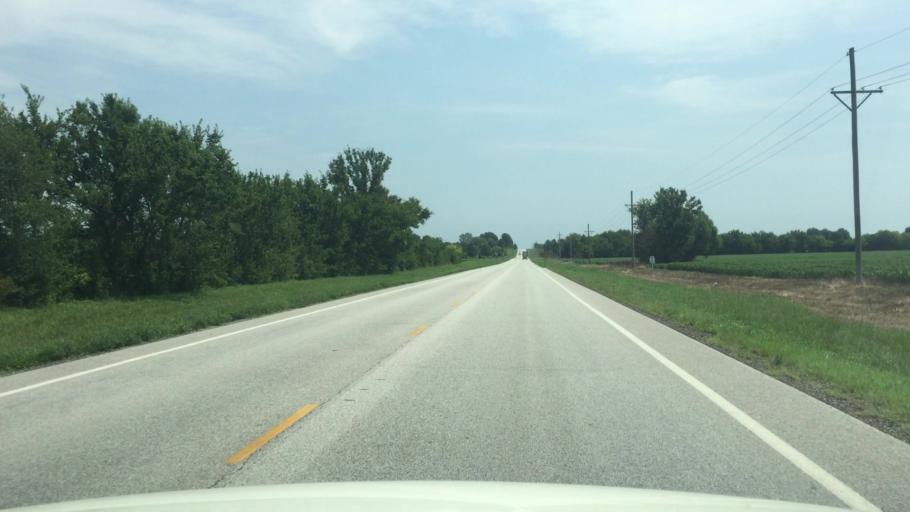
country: US
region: Kansas
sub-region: Cherokee County
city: Columbus
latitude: 37.1780
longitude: -94.8013
